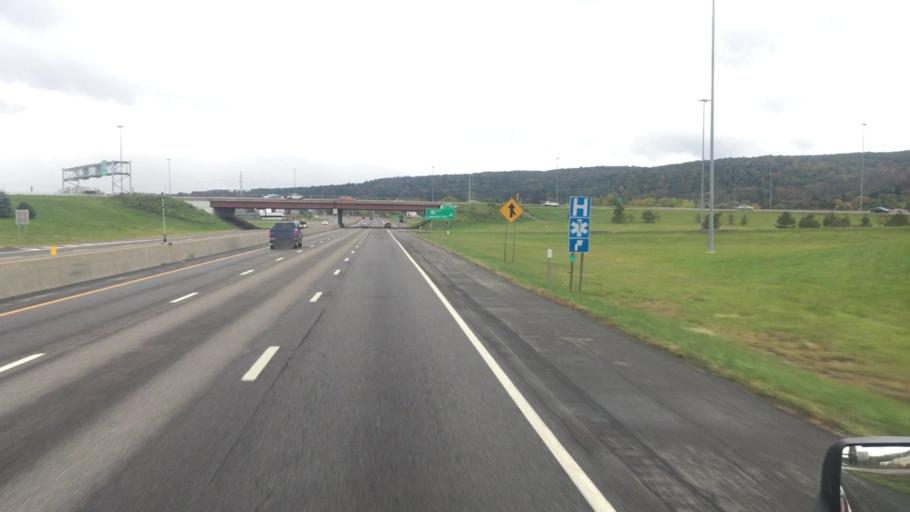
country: US
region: New York
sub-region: Broome County
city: Johnson City
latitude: 42.1199
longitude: -75.9664
